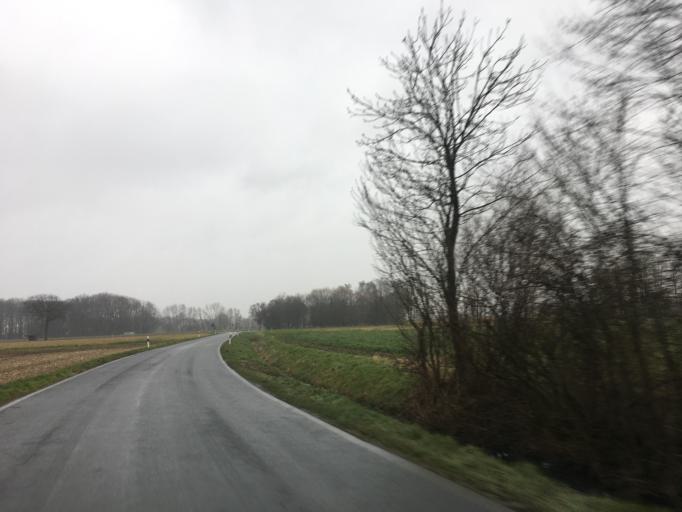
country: DE
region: North Rhine-Westphalia
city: Ludinghausen
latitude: 51.8196
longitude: 7.3732
